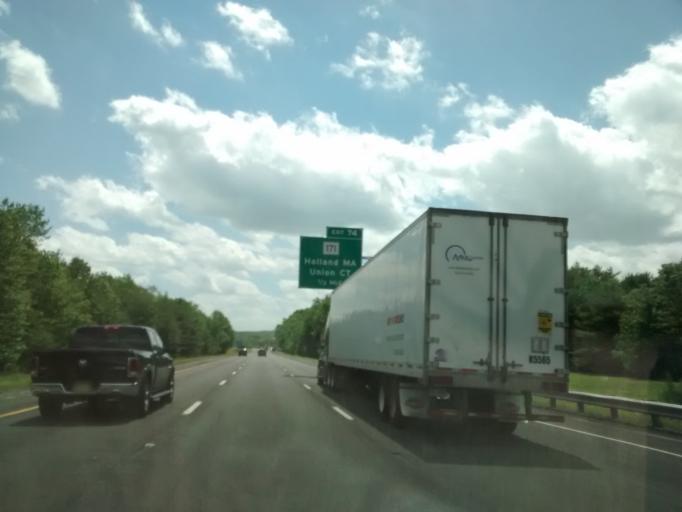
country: US
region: Massachusetts
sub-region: Hampden County
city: Holland
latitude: 42.0339
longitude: -72.1336
